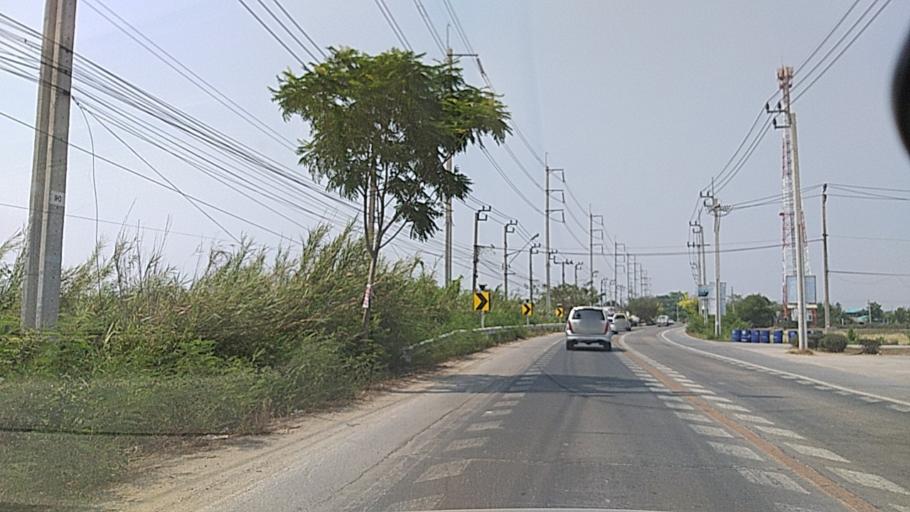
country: TH
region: Nonthaburi
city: Sai Noi
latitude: 13.9423
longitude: 100.3155
